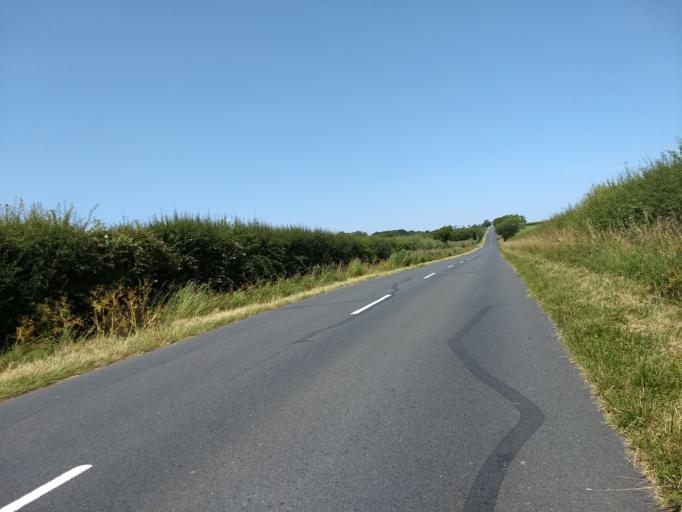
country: GB
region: England
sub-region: Isle of Wight
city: Northwood
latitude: 50.7142
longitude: -1.3514
